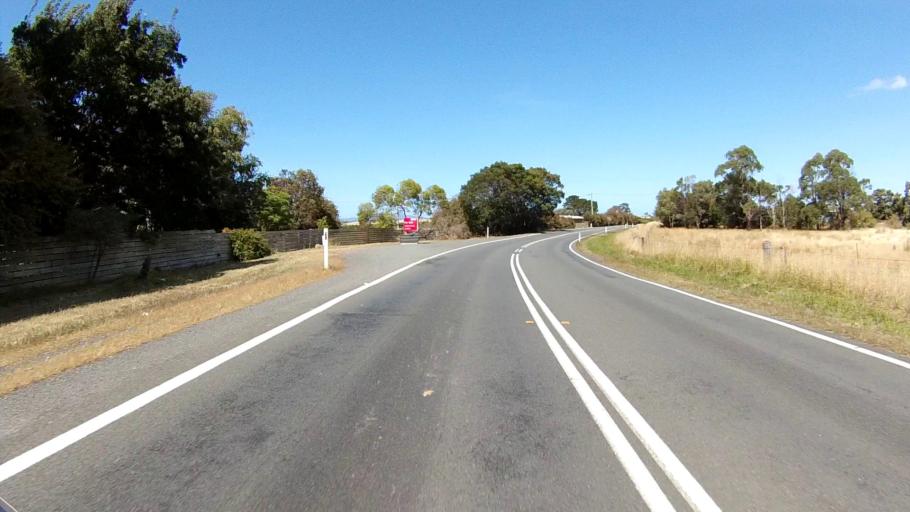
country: AU
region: Tasmania
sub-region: Break O'Day
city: St Helens
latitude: -42.0693
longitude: 148.0651
